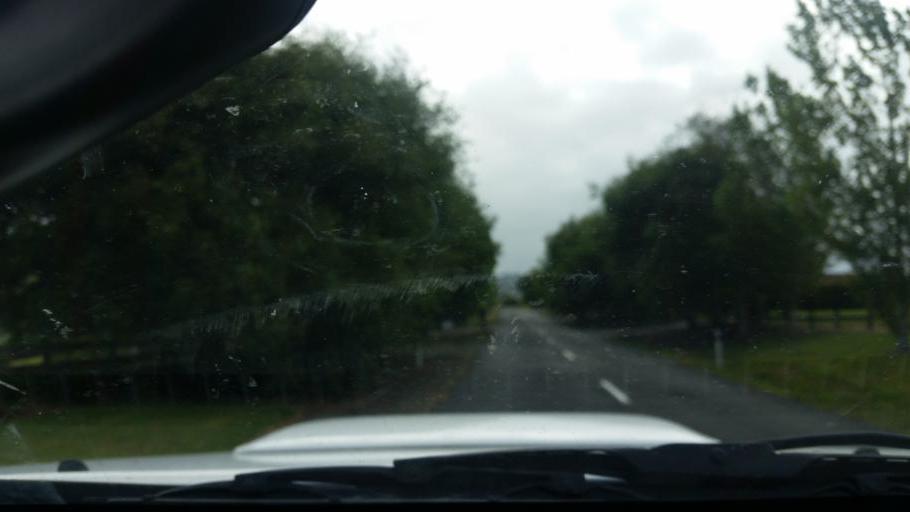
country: NZ
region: Auckland
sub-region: Auckland
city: Wellsford
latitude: -36.1307
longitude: 174.3681
